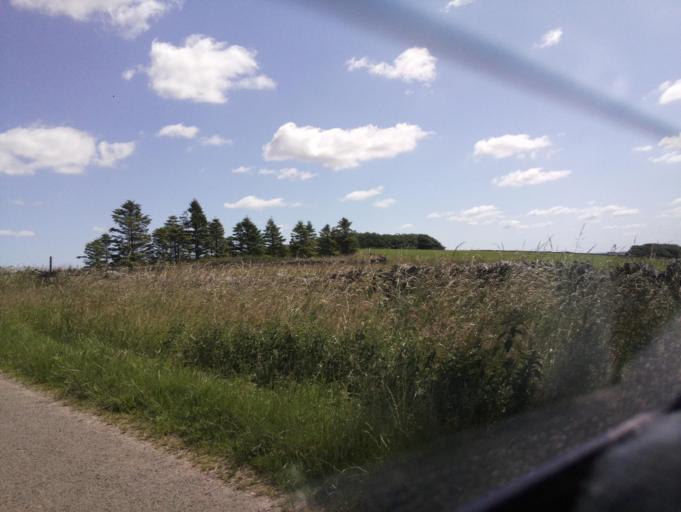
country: GB
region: England
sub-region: Derbyshire
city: Buxton
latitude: 53.1869
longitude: -1.8312
